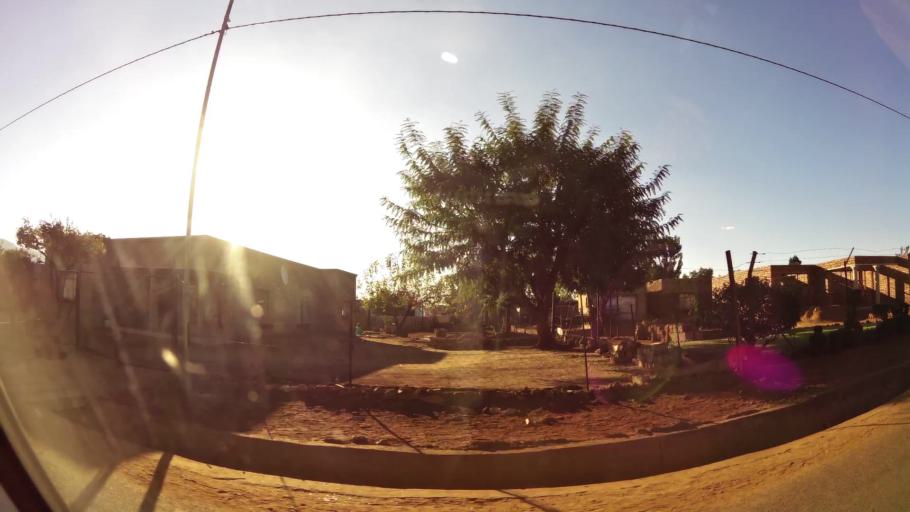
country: ZA
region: Limpopo
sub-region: Waterberg District Municipality
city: Mokopane
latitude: -24.1665
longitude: 28.9876
